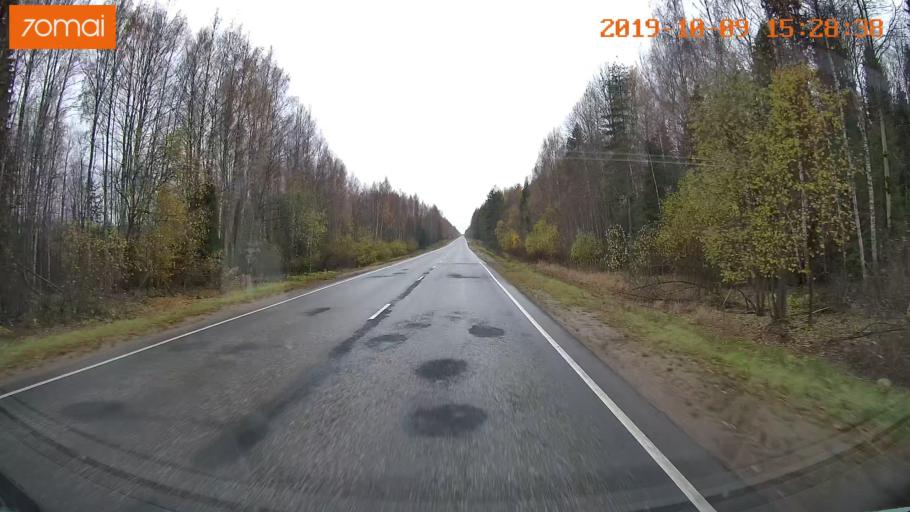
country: RU
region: Kostroma
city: Susanino
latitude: 58.0007
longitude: 41.3565
